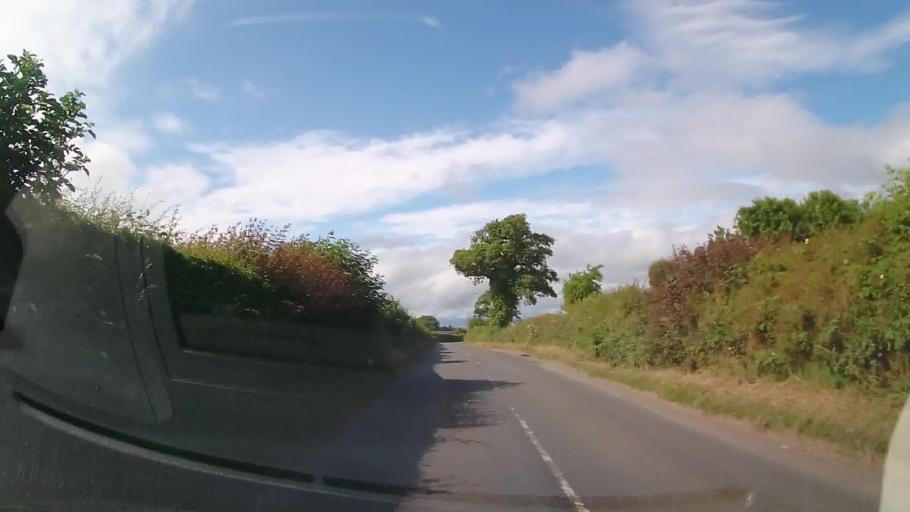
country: GB
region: England
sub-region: Shropshire
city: Petton
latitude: 52.8357
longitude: -2.8052
